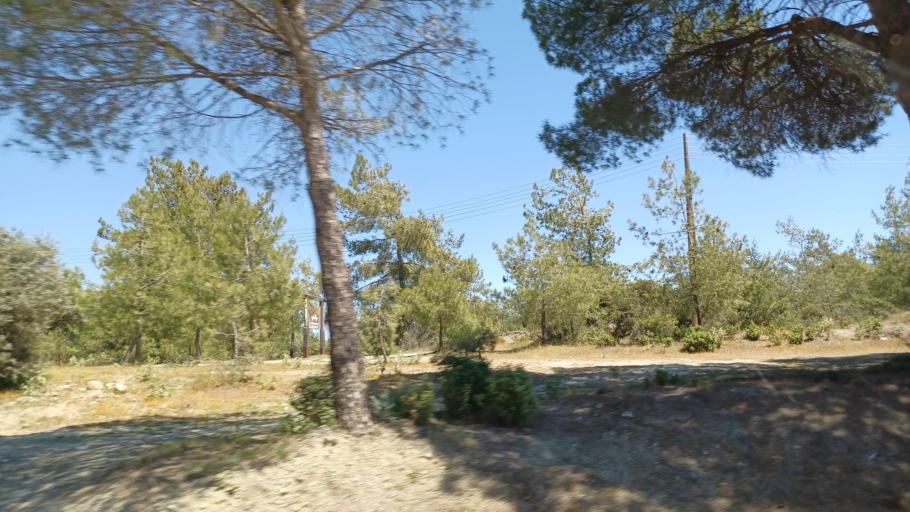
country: CY
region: Limassol
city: Parekklisha
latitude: 34.8088
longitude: 33.1622
